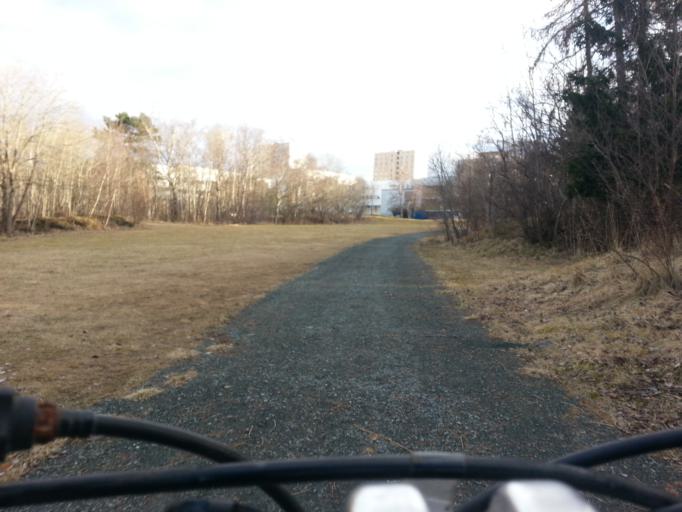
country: NO
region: Sor-Trondelag
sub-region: Trondheim
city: Trondheim
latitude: 63.4563
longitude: 10.4450
